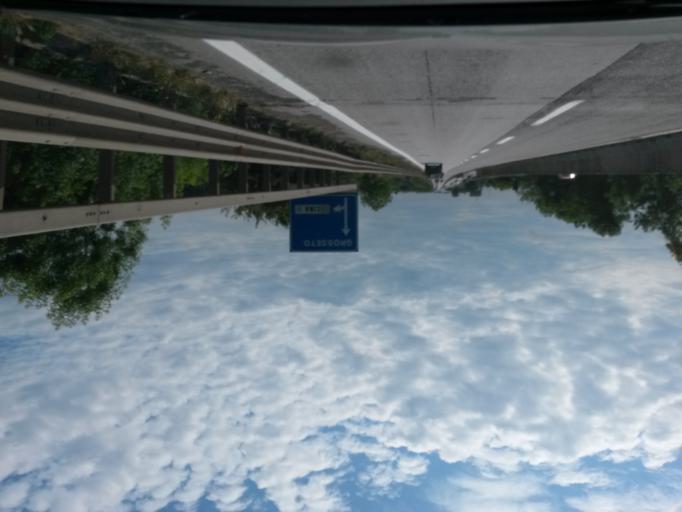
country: IT
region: Tuscany
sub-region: Provincia di Livorno
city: Cecina
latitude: 43.3237
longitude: 10.5306
